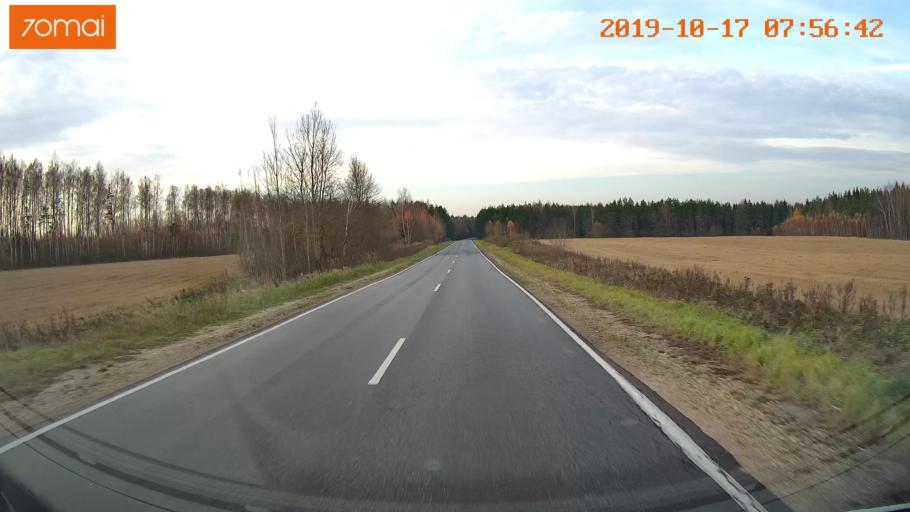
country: RU
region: Vladimir
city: Bavleny
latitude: 56.4198
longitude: 39.5873
